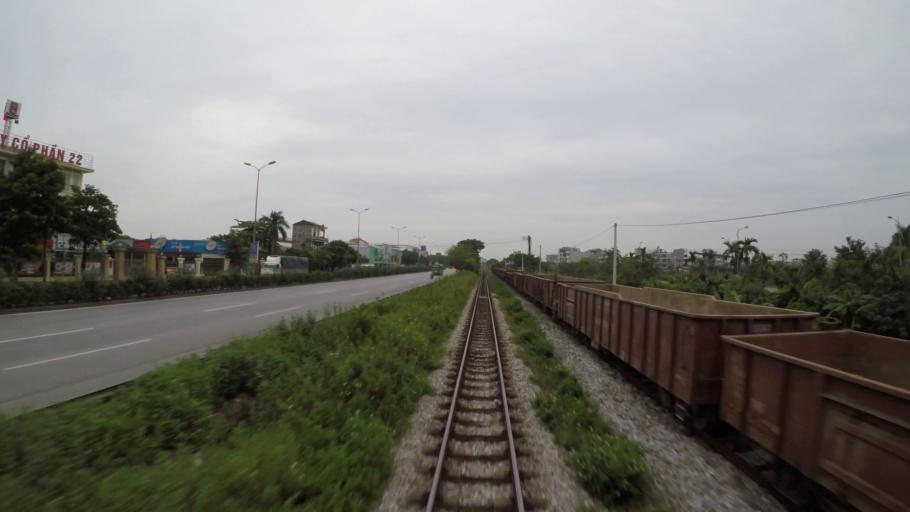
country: VN
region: Hung Yen
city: Nhu Quynh
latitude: 21.0002
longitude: 105.9669
